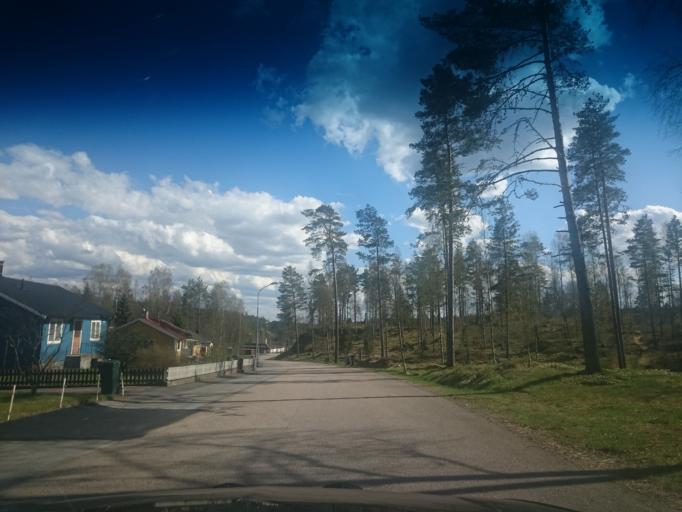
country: SE
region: Kronoberg
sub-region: Vaxjo Kommun
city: Braas
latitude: 57.2236
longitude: 15.1424
